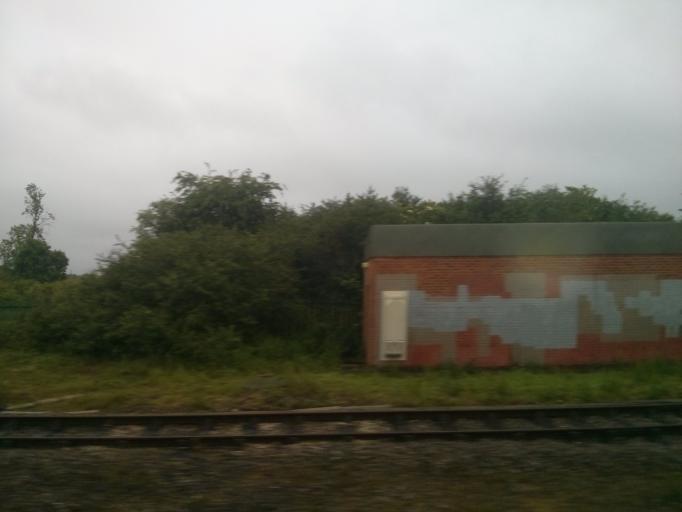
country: GB
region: England
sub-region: West Berkshire
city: Theale
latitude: 51.4090
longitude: -1.1256
